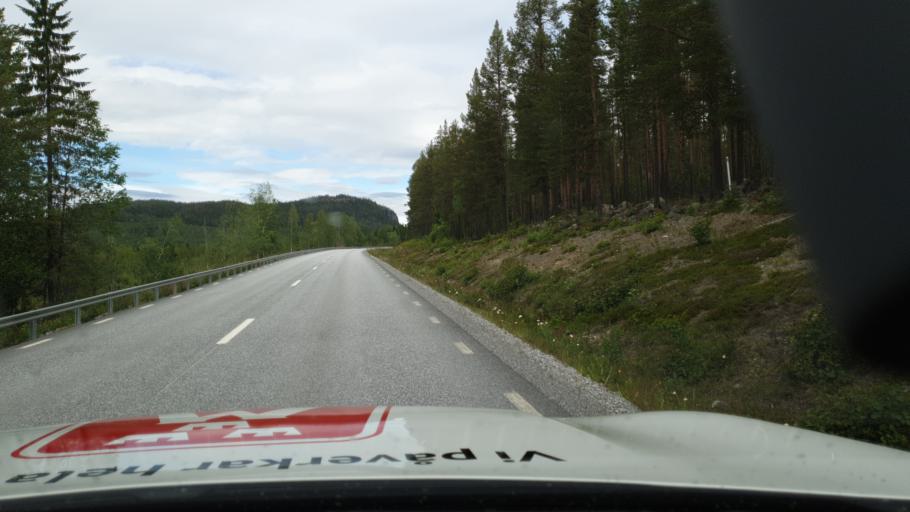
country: SE
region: Vaesterbotten
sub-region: Storumans Kommun
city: Fristad
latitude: 65.2702
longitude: 16.8212
